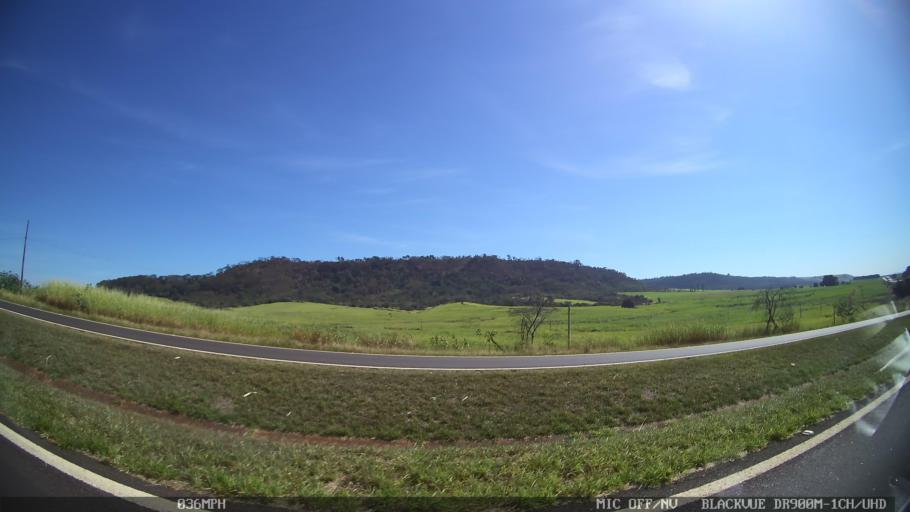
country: BR
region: Sao Paulo
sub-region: Sao Simao
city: Sao Simao
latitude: -21.5271
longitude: -47.6439
